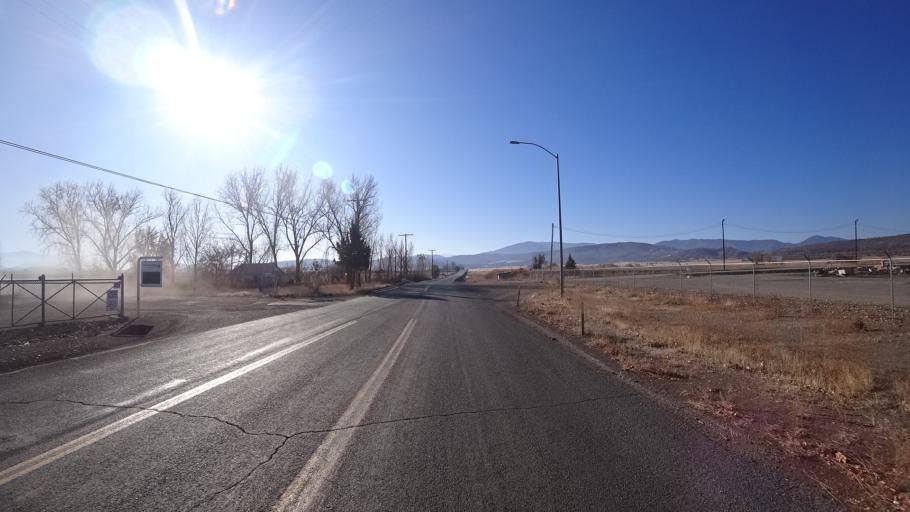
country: US
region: California
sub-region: Siskiyou County
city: Yreka
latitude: 41.7292
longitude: -122.5934
